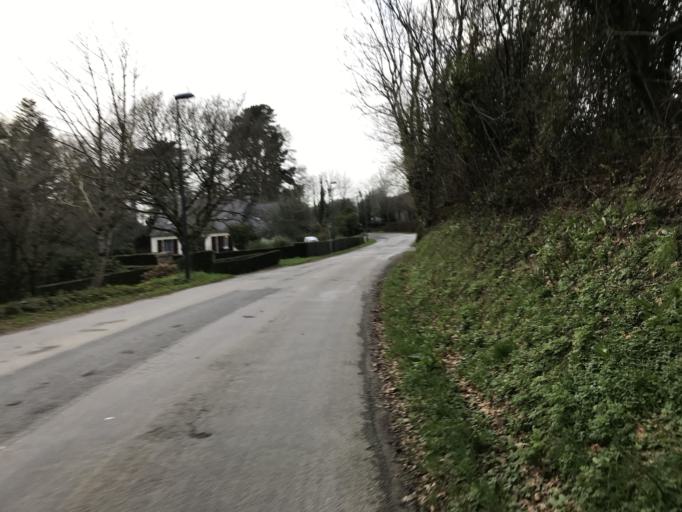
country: FR
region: Brittany
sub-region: Departement du Finistere
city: Daoulas
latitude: 48.3607
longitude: -4.2655
